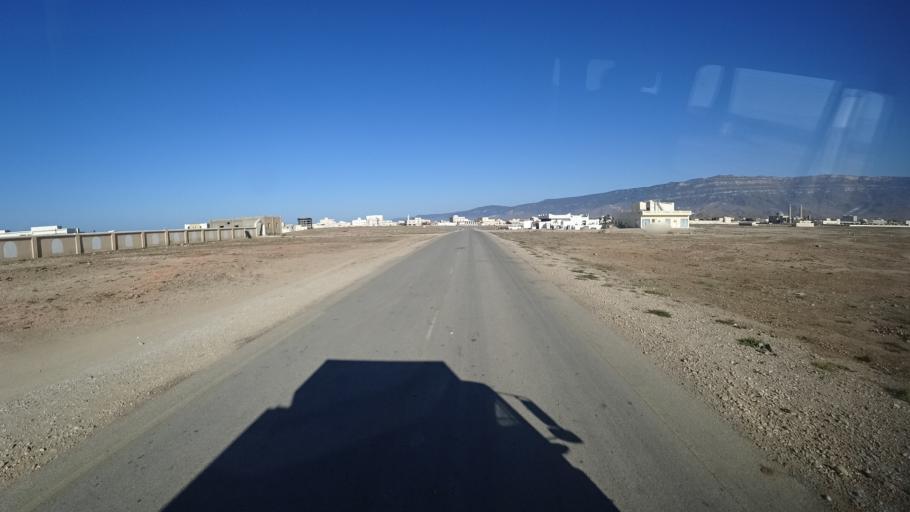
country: OM
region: Zufar
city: Salalah
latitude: 16.9800
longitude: 54.6978
